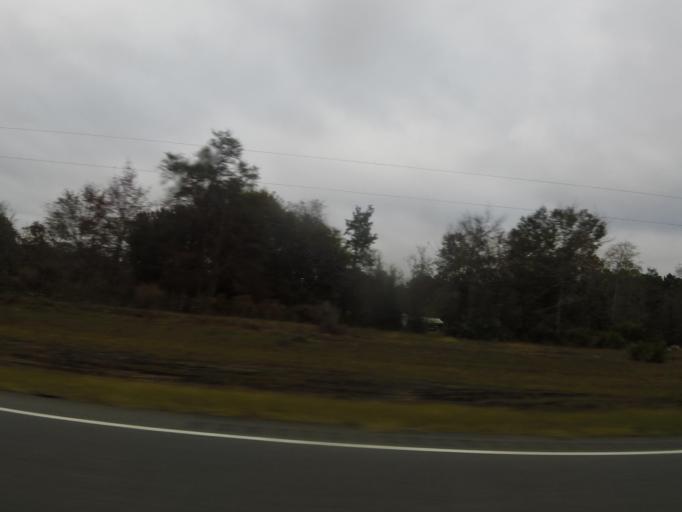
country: US
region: Georgia
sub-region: Charlton County
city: Folkston
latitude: 30.9054
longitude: -82.0684
